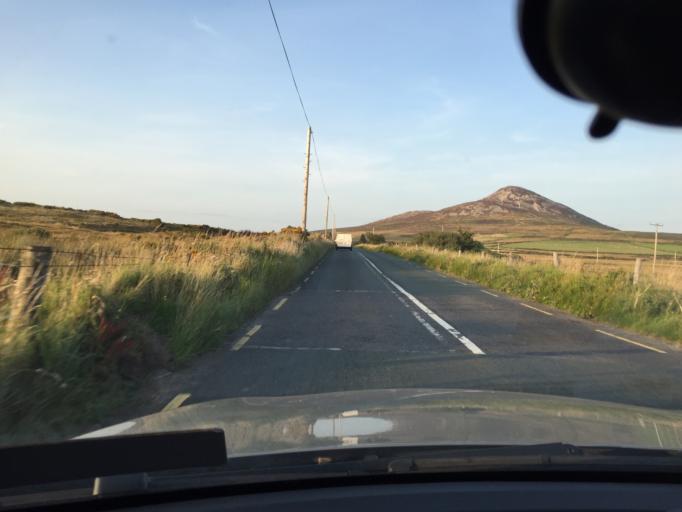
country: IE
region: Leinster
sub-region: Wicklow
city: Kilmacanoge
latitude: 53.1417
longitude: -6.1698
